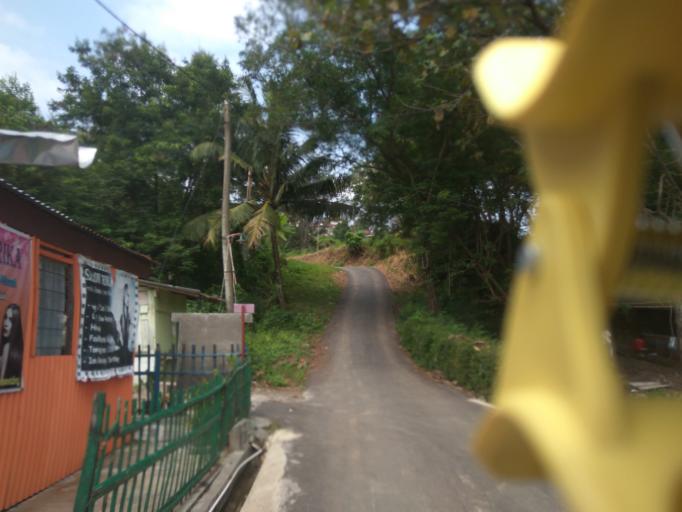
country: ID
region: Central Java
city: Semarang
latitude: -7.0435
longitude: 110.4130
